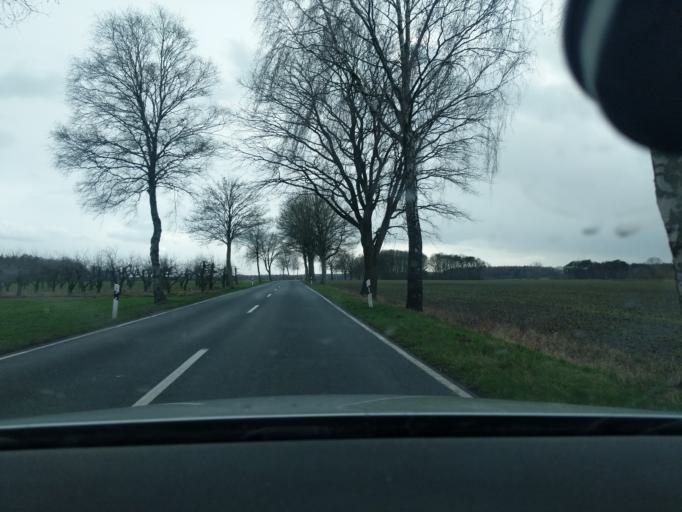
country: DE
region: Lower Saxony
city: Bliedersdorf
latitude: 53.4994
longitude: 9.5376
